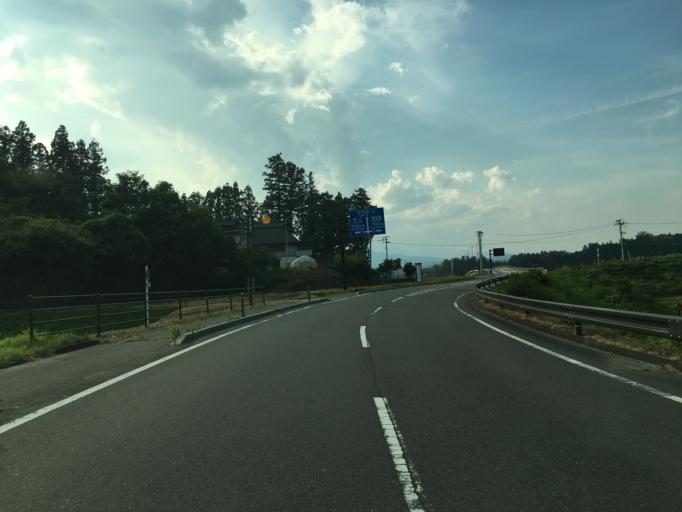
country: JP
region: Fukushima
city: Nihommatsu
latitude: 37.5515
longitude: 140.4374
